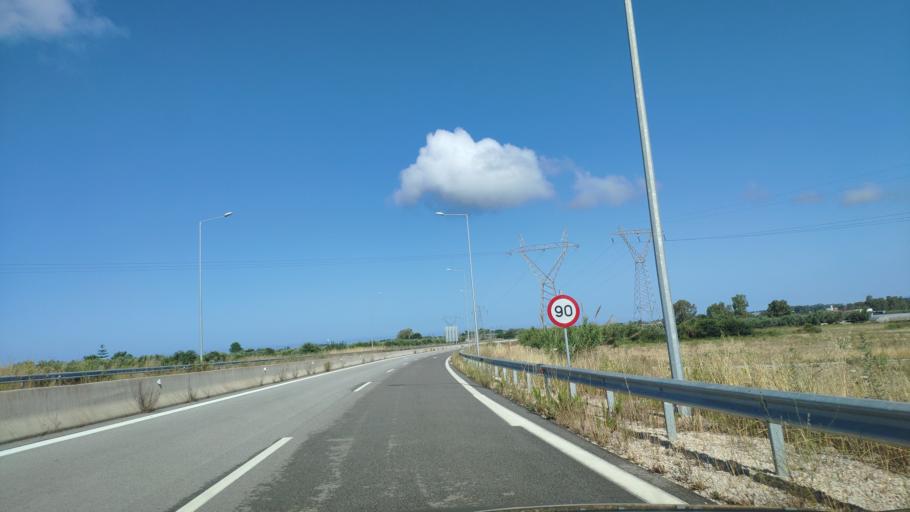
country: GR
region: Epirus
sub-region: Nomos Prevezis
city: Preveza
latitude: 38.9129
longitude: 20.7992
